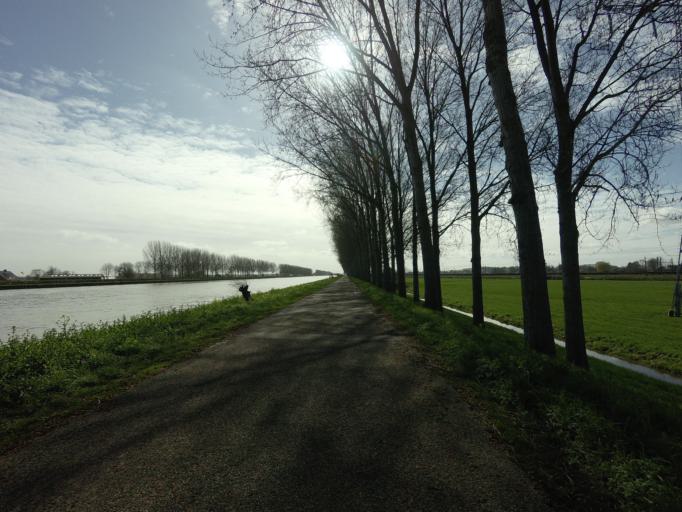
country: NL
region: Utrecht
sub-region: Stichtse Vecht
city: Vreeland
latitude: 52.2422
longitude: 5.0102
